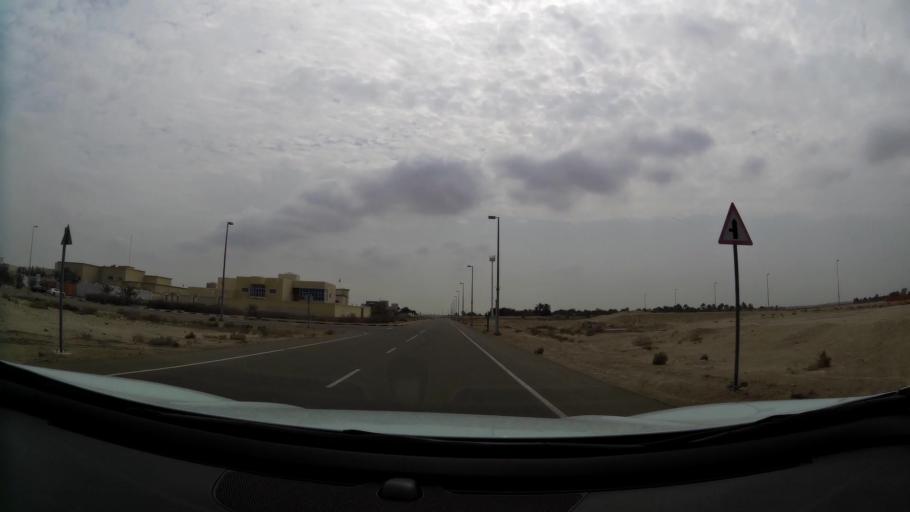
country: AE
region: Abu Dhabi
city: Abu Dhabi
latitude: 24.6313
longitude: 54.6554
